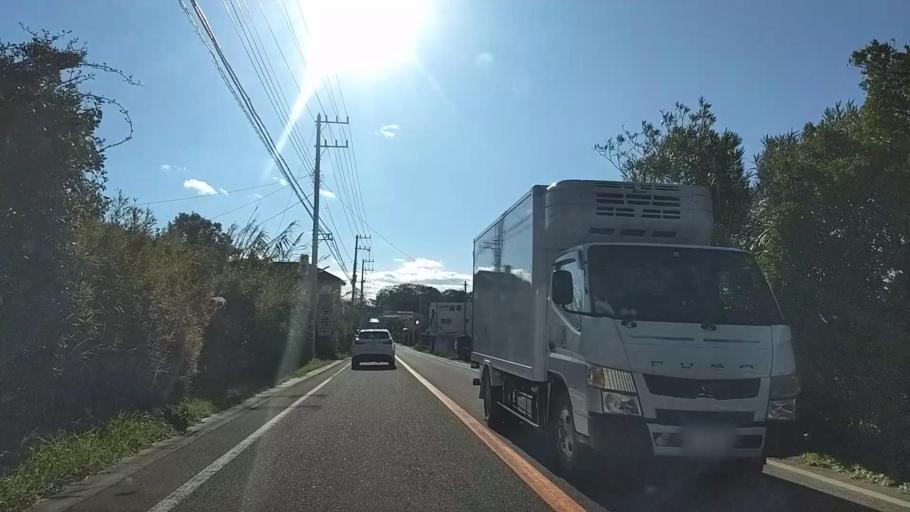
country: JP
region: Chiba
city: Futtsu
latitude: 35.1494
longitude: 139.8307
